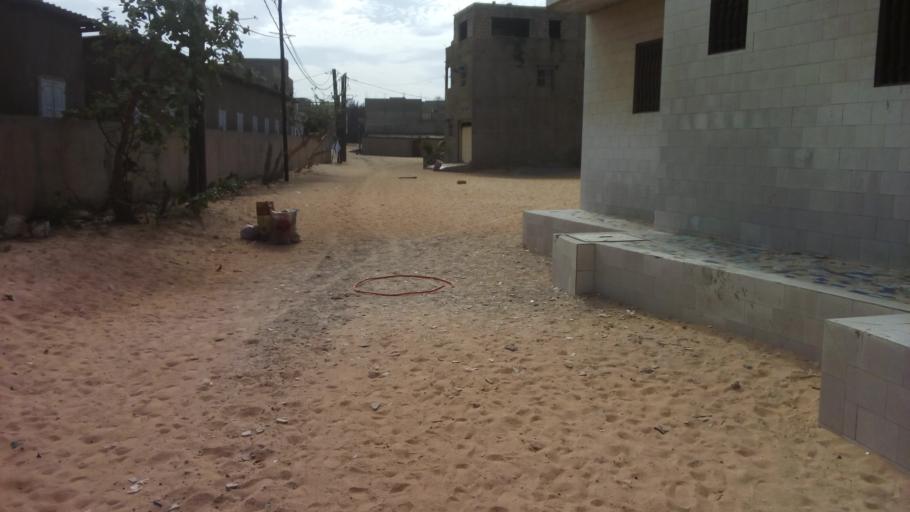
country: SN
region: Dakar
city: Pikine
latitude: 14.8022
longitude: -17.3377
